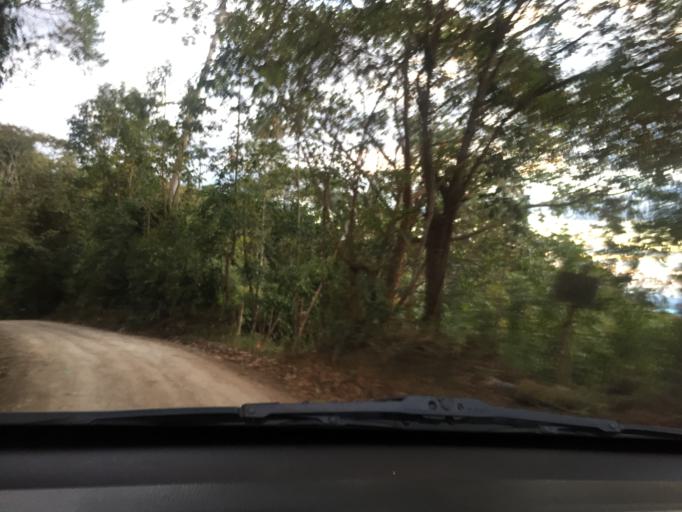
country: CO
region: Cundinamarca
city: Zipacon
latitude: 4.7035
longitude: -74.4088
